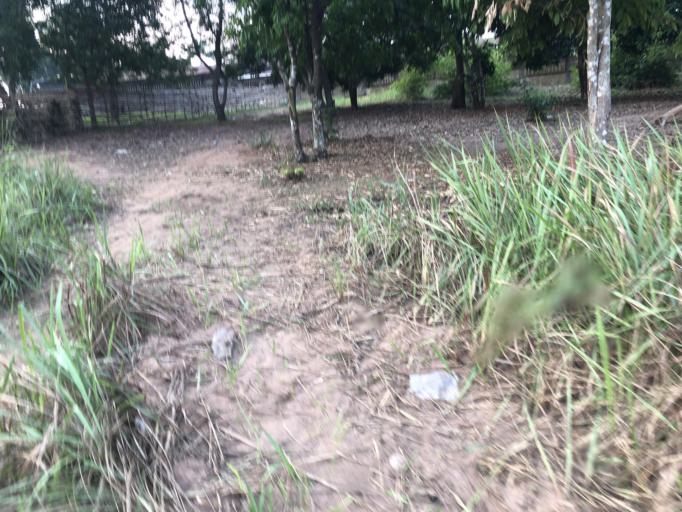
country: CD
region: Bandundu
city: Kikwit
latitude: -5.0727
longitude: 18.8480
